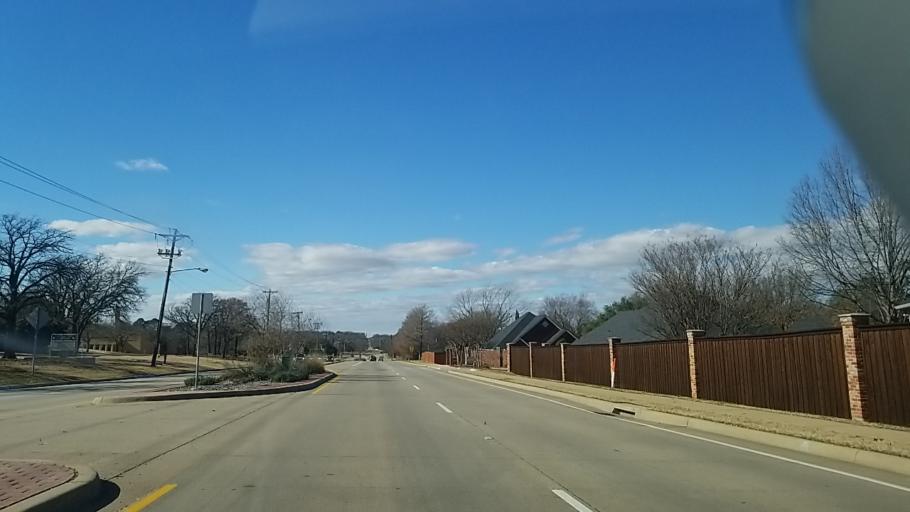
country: US
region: Texas
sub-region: Denton County
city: Denton
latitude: 33.1760
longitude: -97.1153
